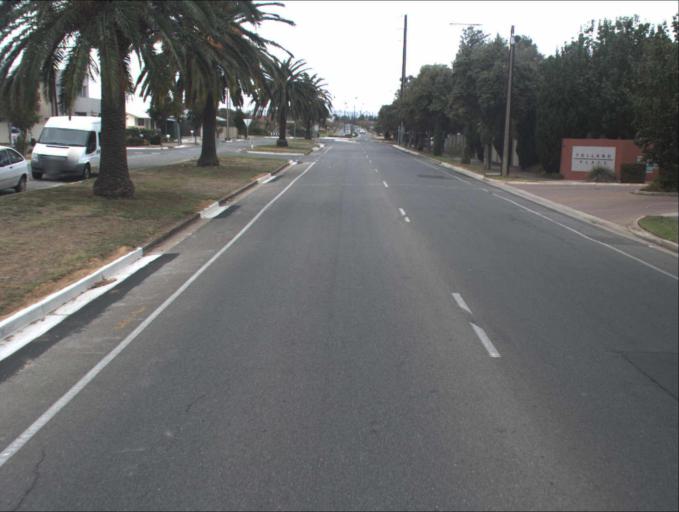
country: AU
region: South Australia
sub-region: Port Adelaide Enfield
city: Klemzig
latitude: -34.8584
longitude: 138.6253
